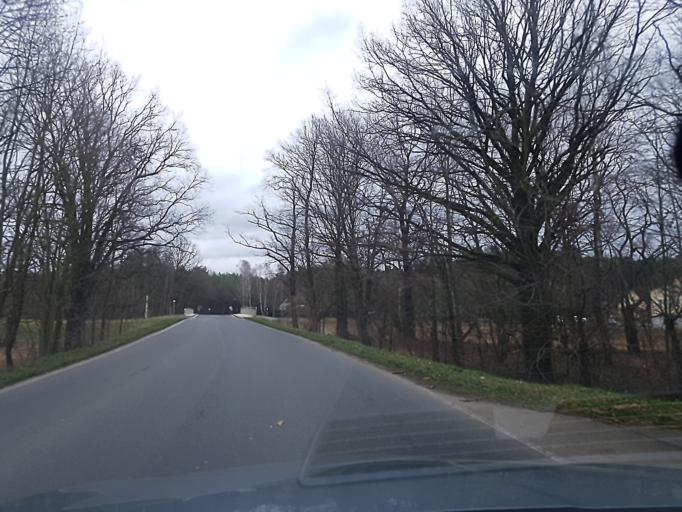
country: DE
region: Brandenburg
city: Bad Liebenwerda
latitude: 51.5493
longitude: 13.3680
